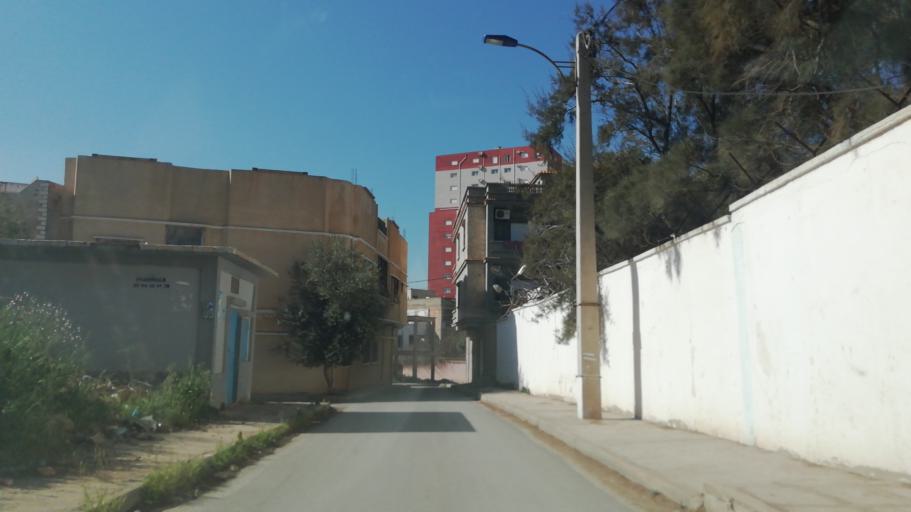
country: DZ
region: Oran
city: Bir el Djir
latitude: 35.7225
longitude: -0.5818
